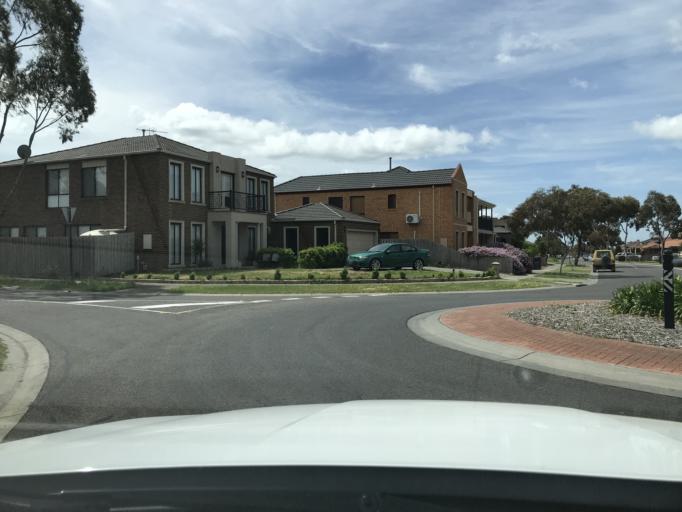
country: AU
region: Victoria
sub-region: Hume
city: Roxburgh Park
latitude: -37.6140
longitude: 144.9310
